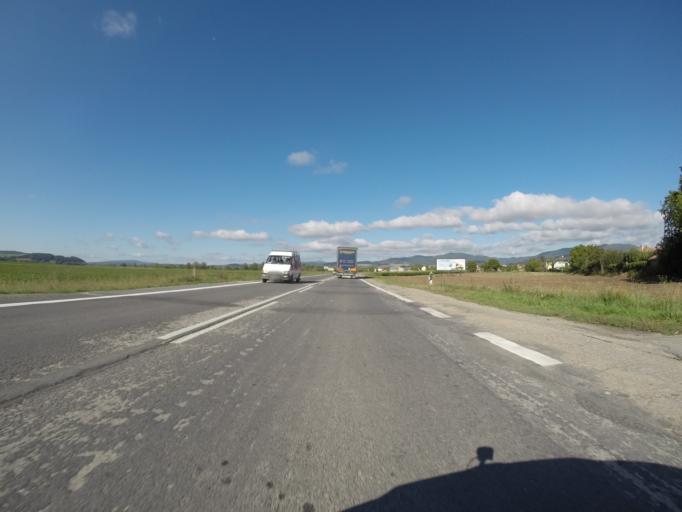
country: SK
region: Trenciansky
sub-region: Okres Trencin
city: Trencin
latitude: 48.8491
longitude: 17.9840
